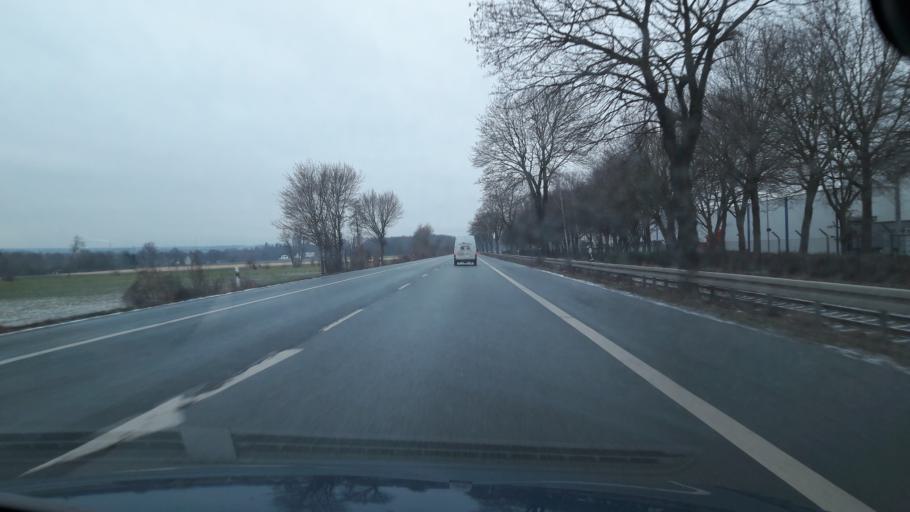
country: DE
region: North Rhine-Westphalia
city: Erwitte
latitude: 51.6290
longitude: 8.3402
